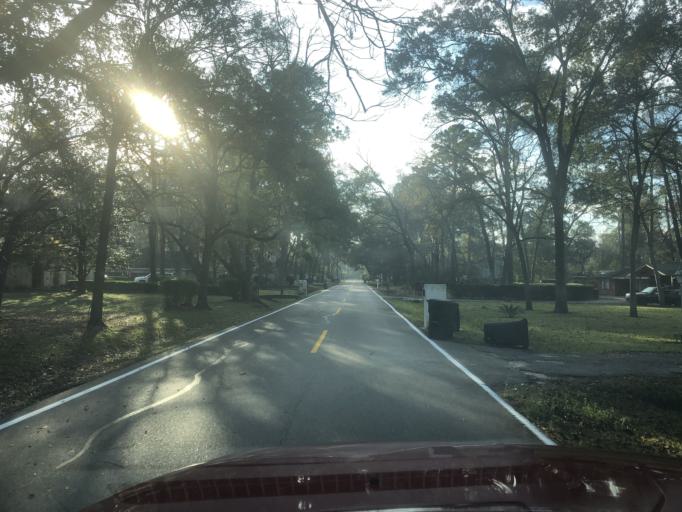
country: US
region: Texas
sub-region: Harris County
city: Spring
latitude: 30.0118
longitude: -95.4756
